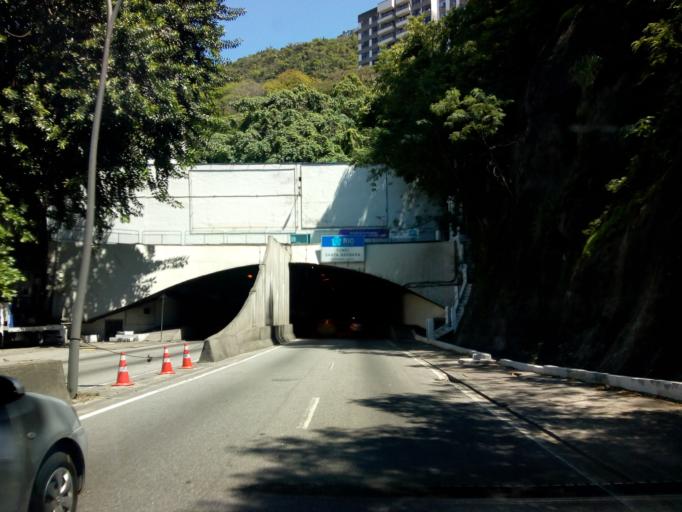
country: BR
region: Rio de Janeiro
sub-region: Rio De Janeiro
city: Rio de Janeiro
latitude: -22.9308
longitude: -43.1859
